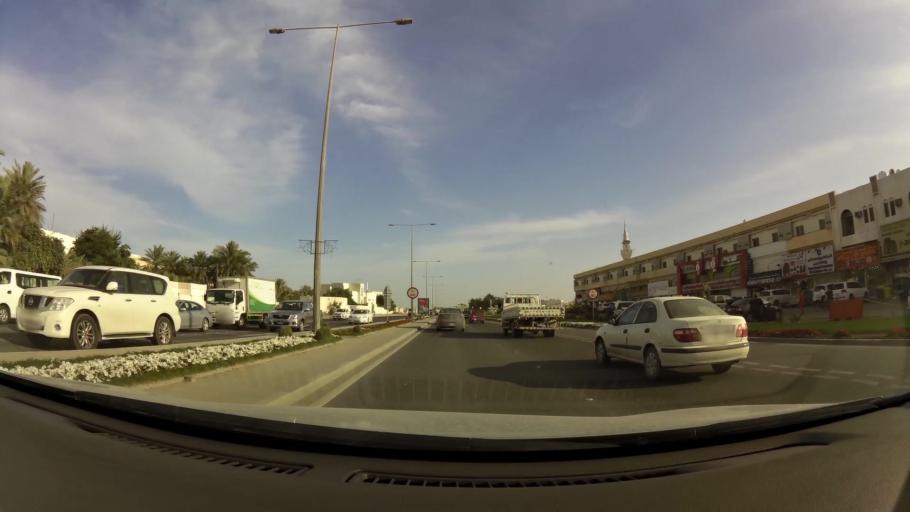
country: QA
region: Al Wakrah
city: Al Wakrah
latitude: 25.1764
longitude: 51.6051
